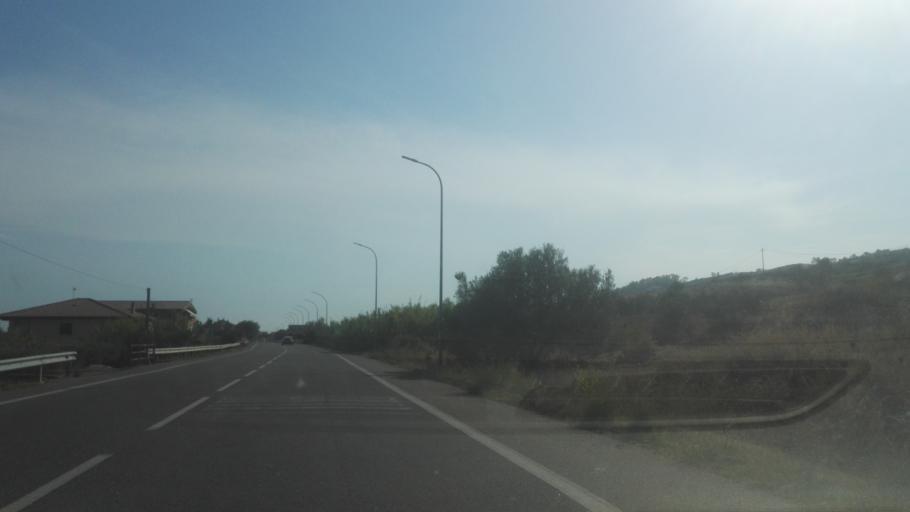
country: IT
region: Calabria
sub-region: Provincia di Reggio Calabria
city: Riace Marina
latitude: 38.4041
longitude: 16.5464
